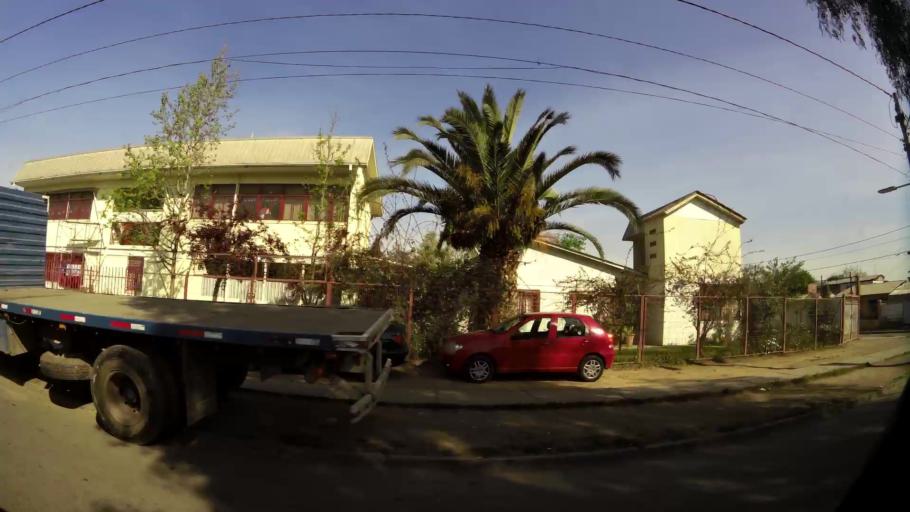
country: CL
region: Santiago Metropolitan
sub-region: Provincia de Santiago
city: Lo Prado
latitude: -33.4165
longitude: -70.7451
